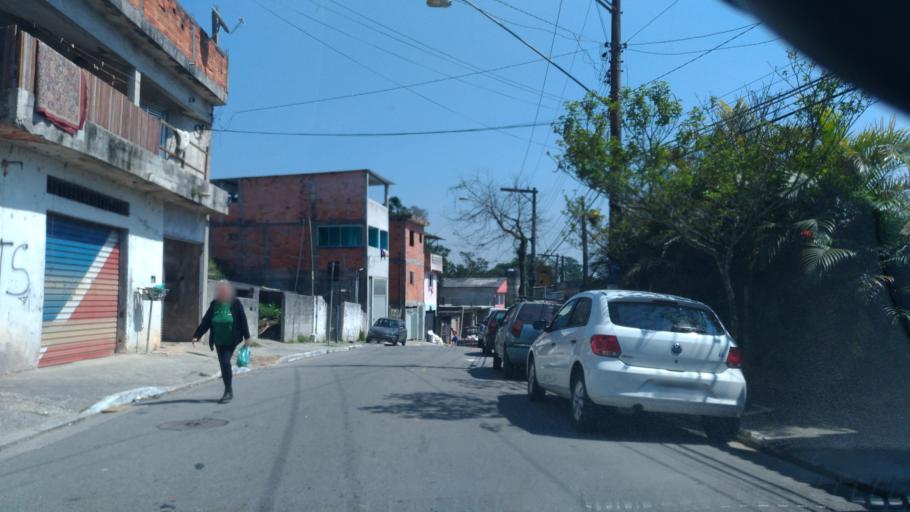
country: BR
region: Sao Paulo
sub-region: Sao Bernardo Do Campo
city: Sao Bernardo do Campo
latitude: -23.7762
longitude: -46.5201
